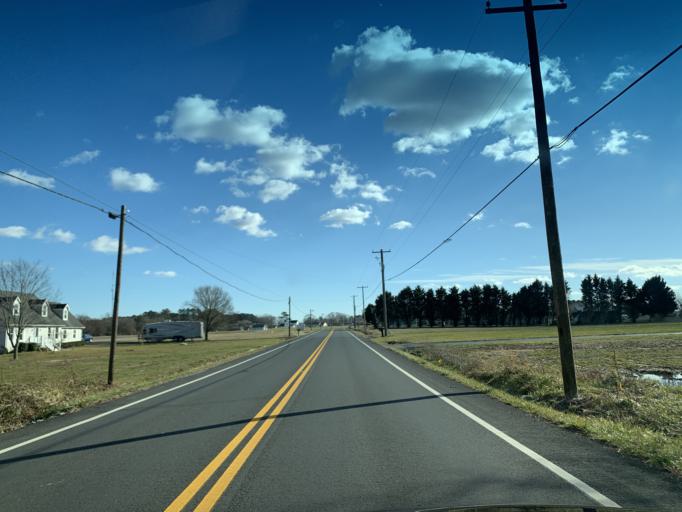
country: US
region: Maryland
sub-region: Worcester County
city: Berlin
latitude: 38.3527
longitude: -75.1946
